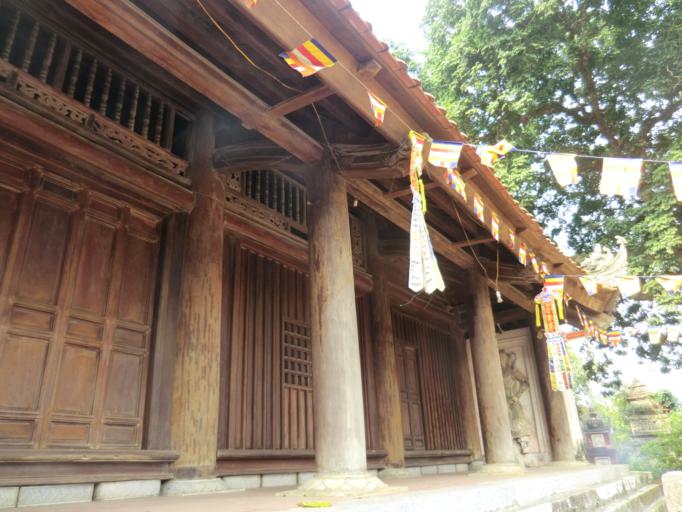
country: VN
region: Ha Noi
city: Chuc Son
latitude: 20.9502
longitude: 105.6799
